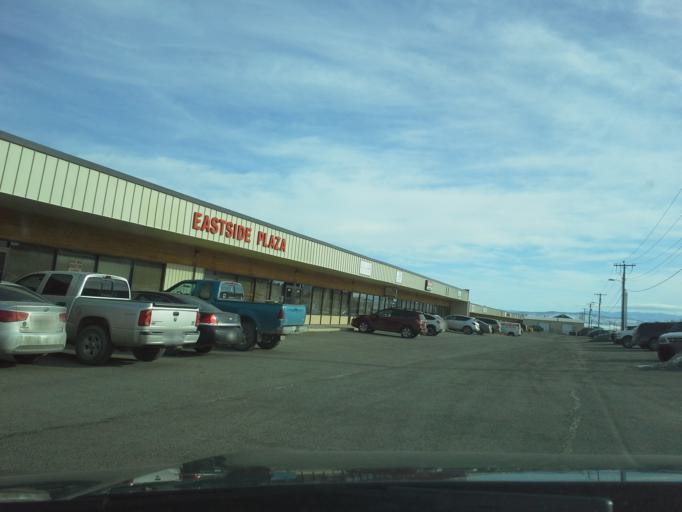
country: US
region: Montana
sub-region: Lewis and Clark County
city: Helena
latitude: 46.5945
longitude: -111.9918
